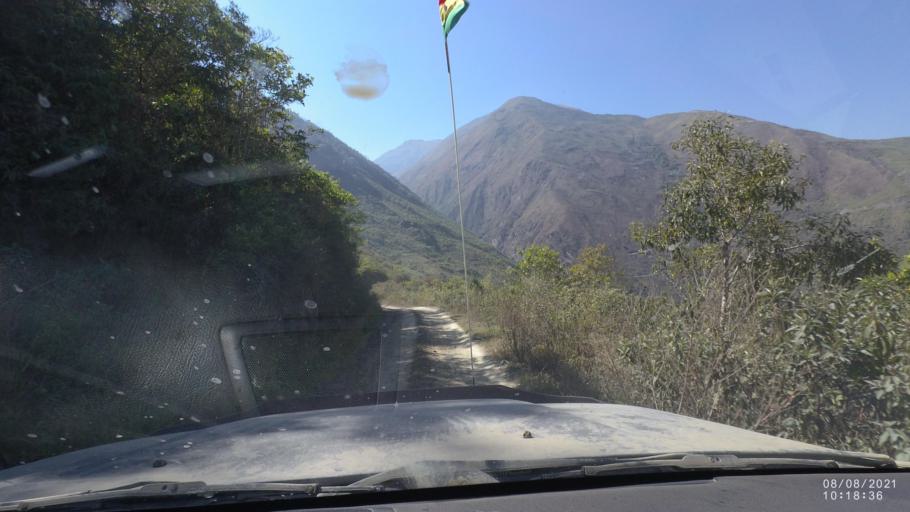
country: BO
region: La Paz
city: Quime
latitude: -16.6858
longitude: -66.7302
